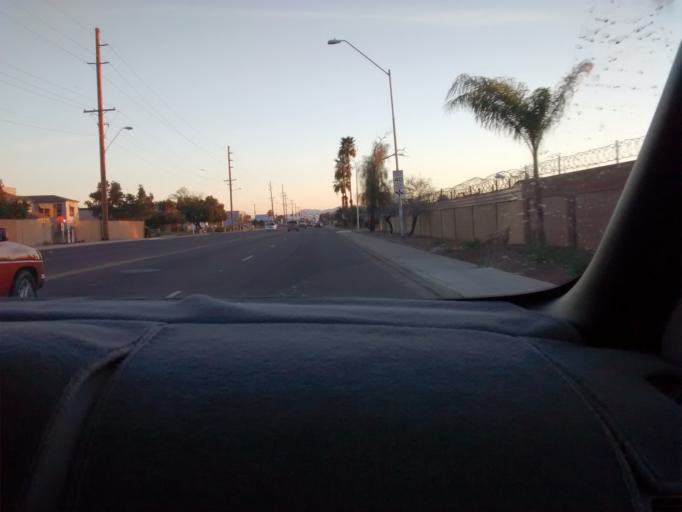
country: US
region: Arizona
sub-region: Maricopa County
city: Glendale
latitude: 33.5487
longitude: -112.2031
